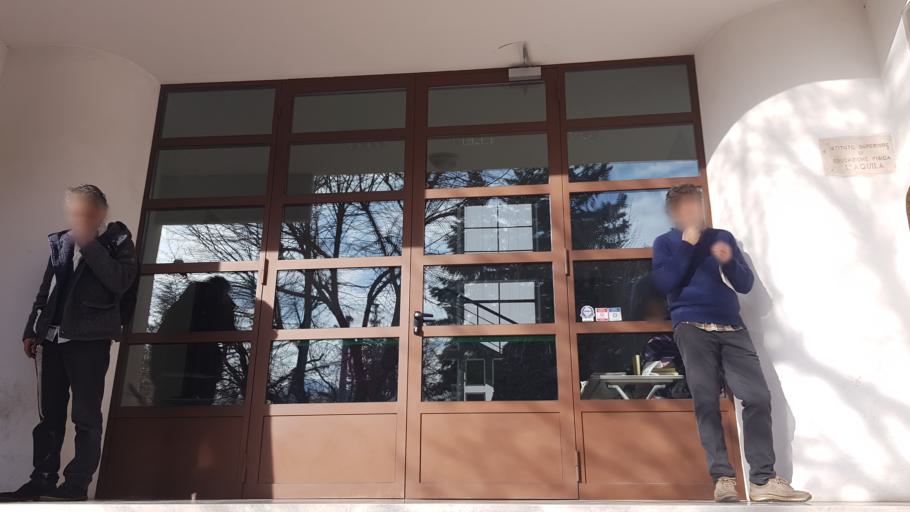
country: IT
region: Abruzzo
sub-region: Provincia dell' Aquila
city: L'Aquila
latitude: 42.3446
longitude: 13.3966
